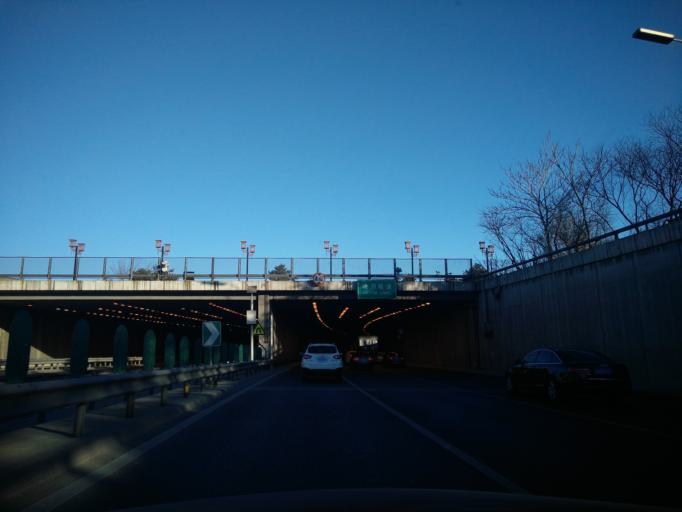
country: CN
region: Beijing
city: Lugu
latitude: 39.8480
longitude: 116.2159
